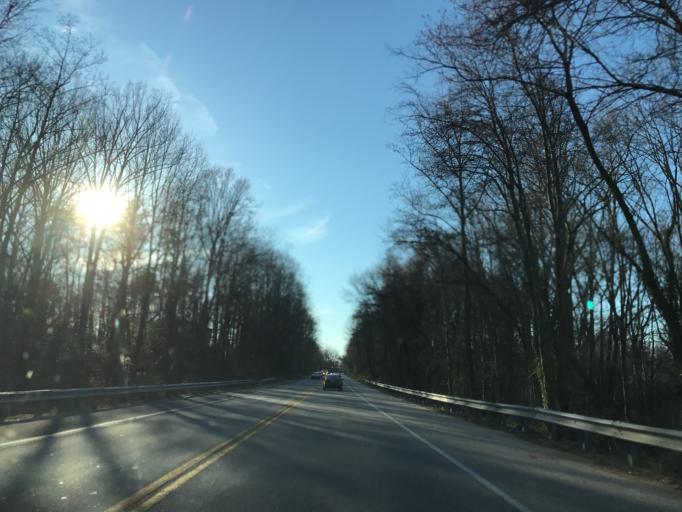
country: US
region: Maryland
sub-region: Anne Arundel County
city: Arnold
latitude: 39.0375
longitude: -76.4830
